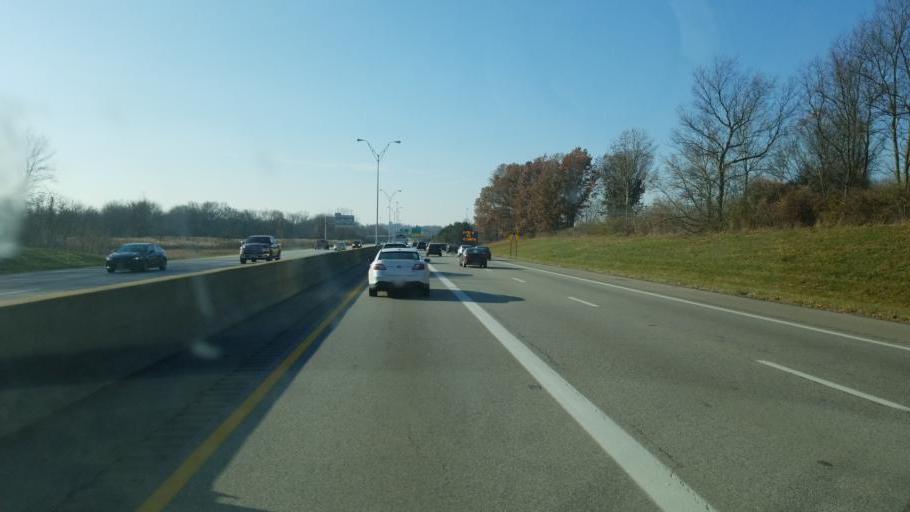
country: US
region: Ohio
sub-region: Summit County
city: Portage Lakes
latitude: 41.0354
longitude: -81.5573
